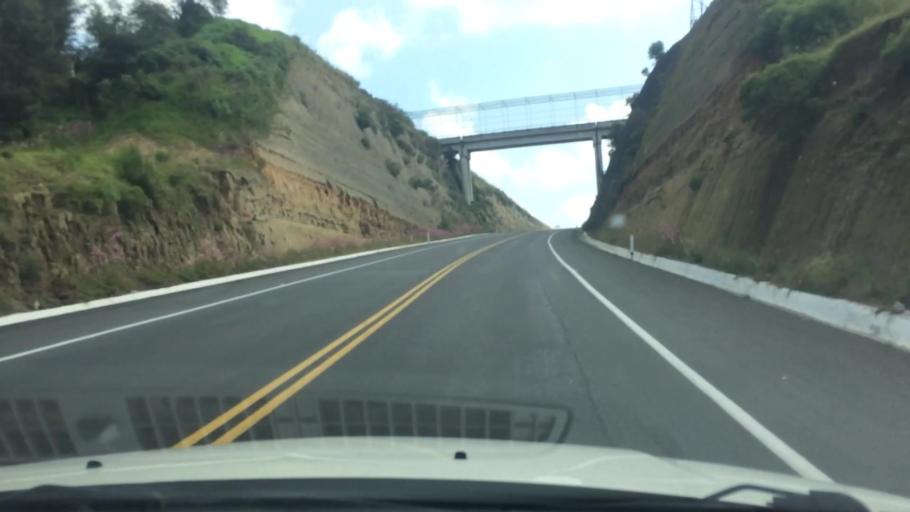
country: MX
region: Mexico
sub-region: Villa Victoria
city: Colonia Doctor Gustavo Baz
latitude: 19.3698
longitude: -99.9373
